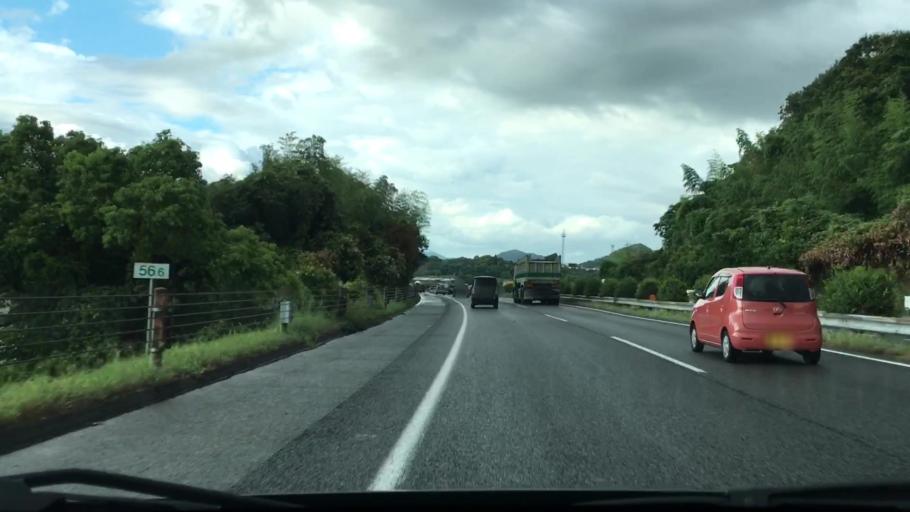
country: JP
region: Fukuoka
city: Koga
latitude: 33.7258
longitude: 130.5030
